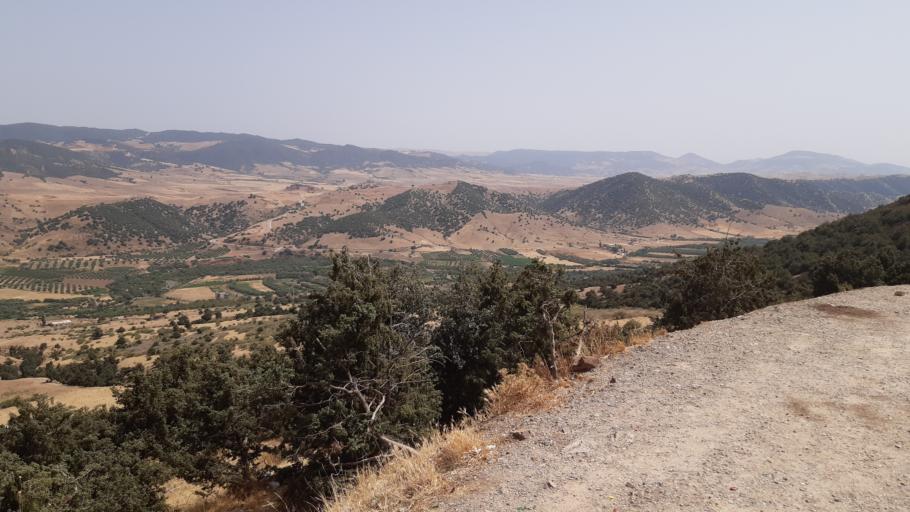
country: MA
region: Meknes-Tafilalet
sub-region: Khenifra
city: Khenifra
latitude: 33.0866
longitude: -5.5422
